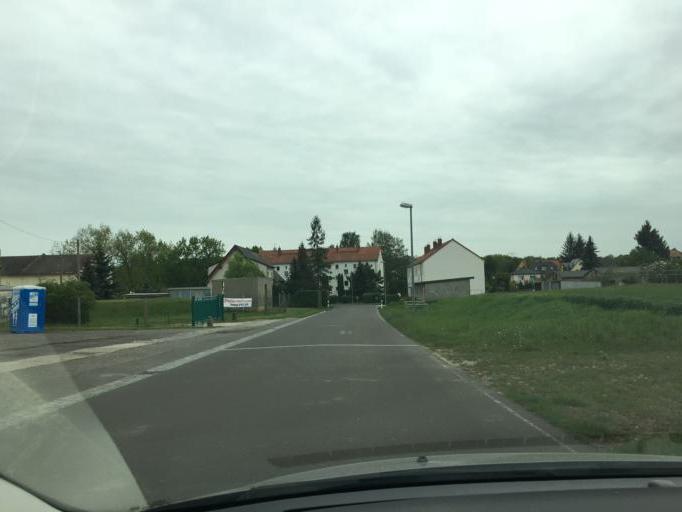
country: DE
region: Saxony
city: Taucha
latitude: 51.3939
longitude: 12.4498
